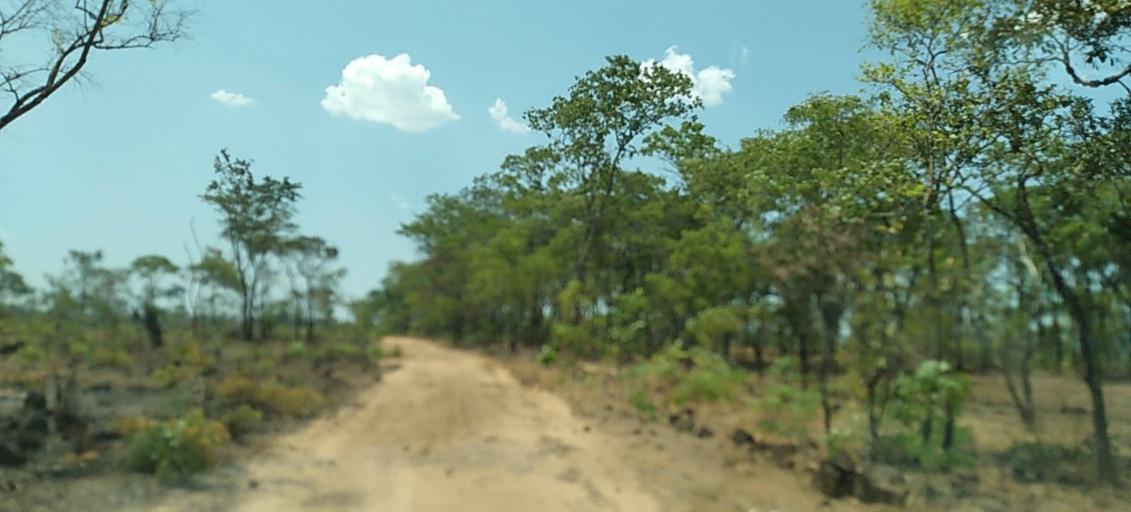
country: ZM
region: Central
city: Kapiri Mposhi
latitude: -13.6561
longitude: 28.4890
